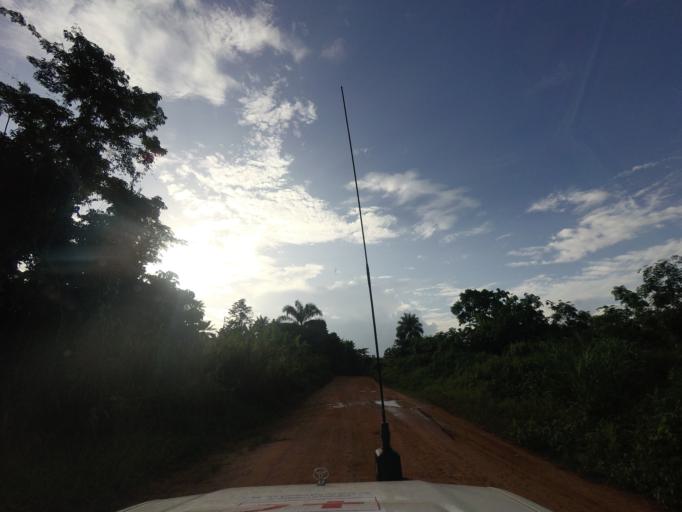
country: GN
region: Nzerekore
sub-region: Nzerekore Prefecture
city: Nzerekore
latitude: 7.6730
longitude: -8.8108
